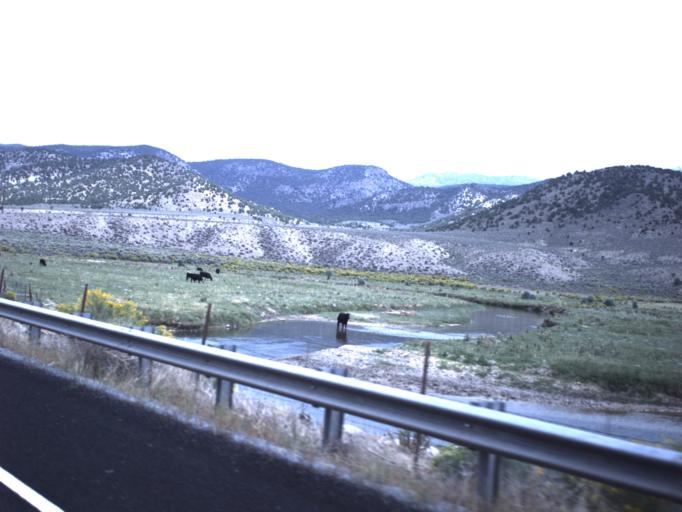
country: US
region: Utah
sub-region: Garfield County
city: Panguitch
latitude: 38.0242
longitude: -112.3599
